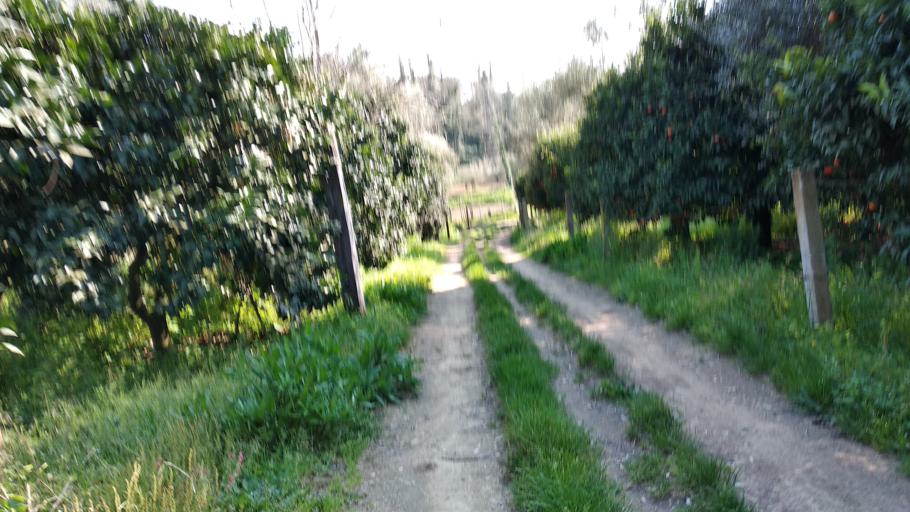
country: IT
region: Calabria
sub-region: Provincia di Reggio Calabria
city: Rizziconi
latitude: 38.4300
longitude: 15.9596
